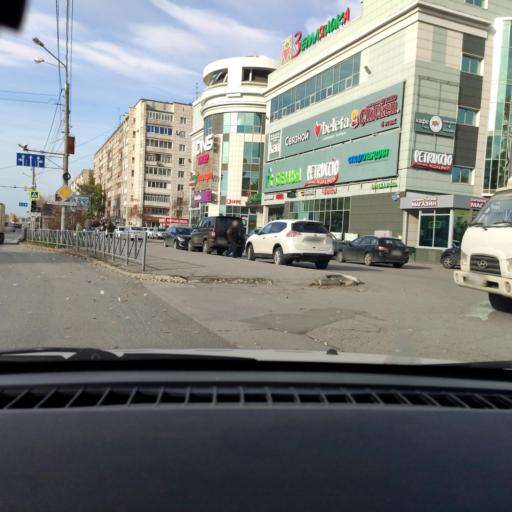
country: RU
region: Perm
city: Kondratovo
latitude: 57.9988
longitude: 56.1563
